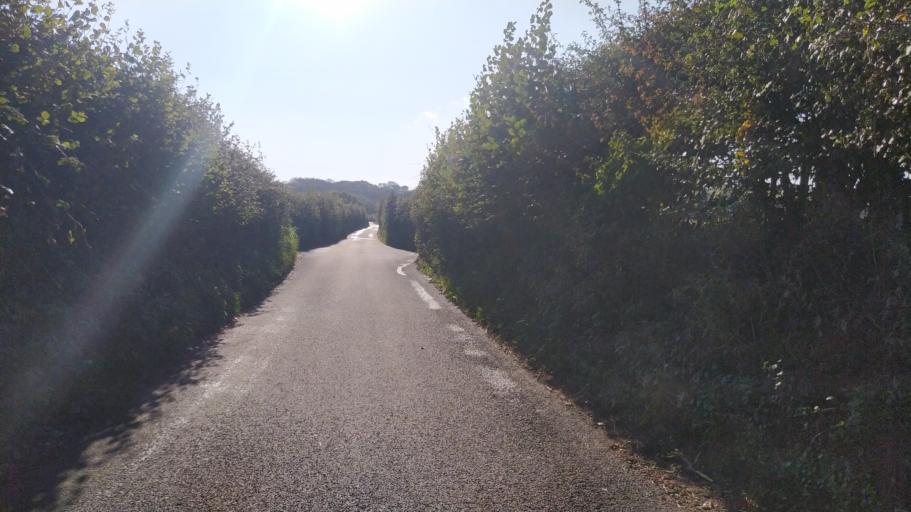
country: GB
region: England
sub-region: Isle of Wight
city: Newport
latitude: 50.6922
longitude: -1.3470
